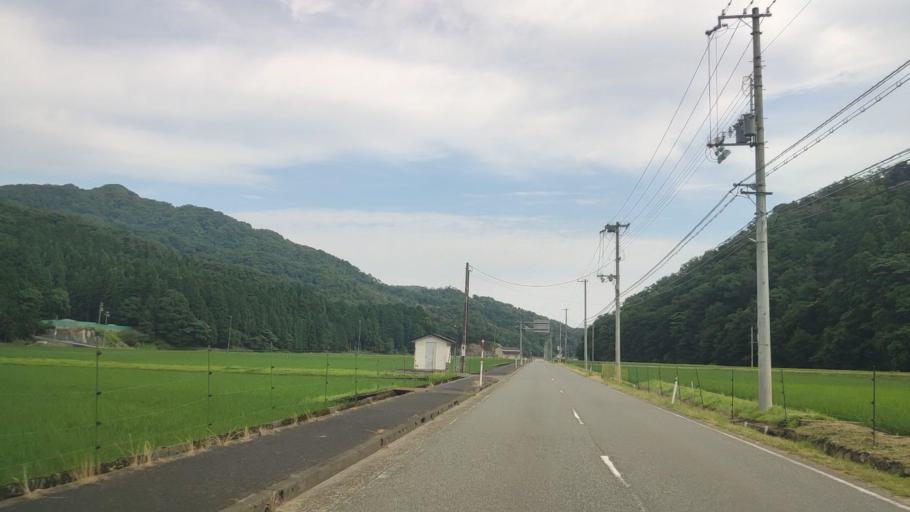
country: JP
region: Hyogo
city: Toyooka
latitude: 35.6160
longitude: 134.8437
